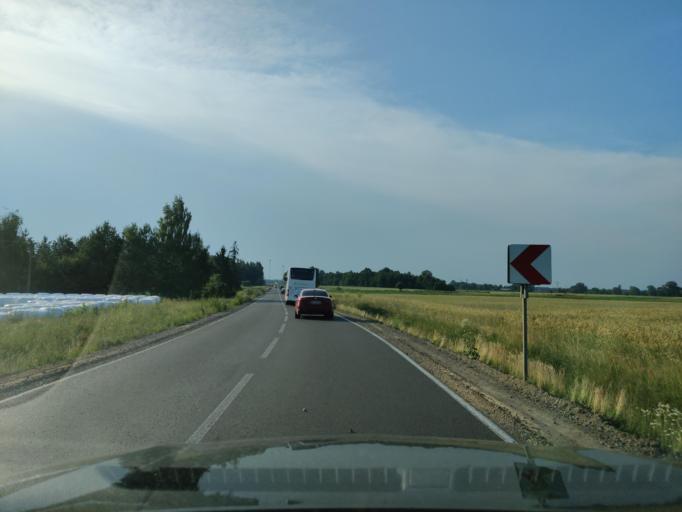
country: PL
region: Masovian Voivodeship
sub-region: Powiat plonski
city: Baboszewo
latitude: 52.7102
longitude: 20.3373
